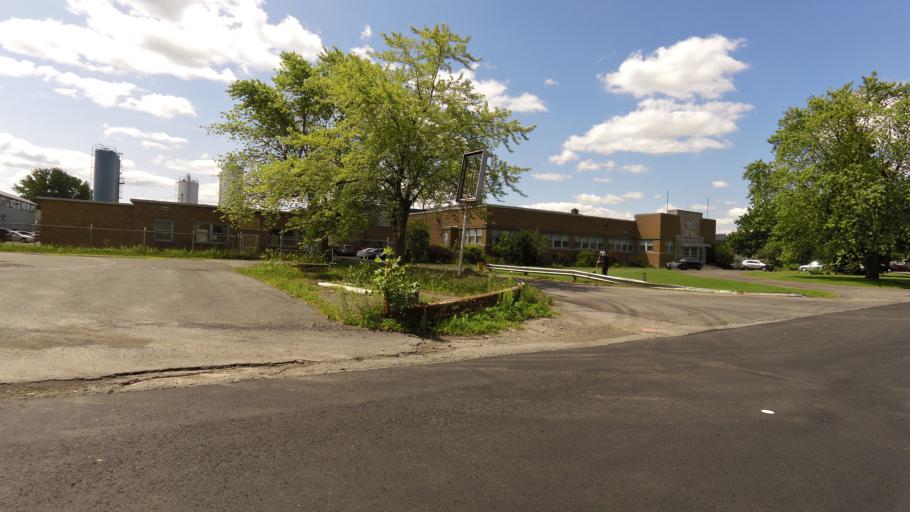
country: CA
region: Quebec
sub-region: Monteregie
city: Saint-Jean-sur-Richelieu
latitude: 45.2944
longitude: -73.2583
